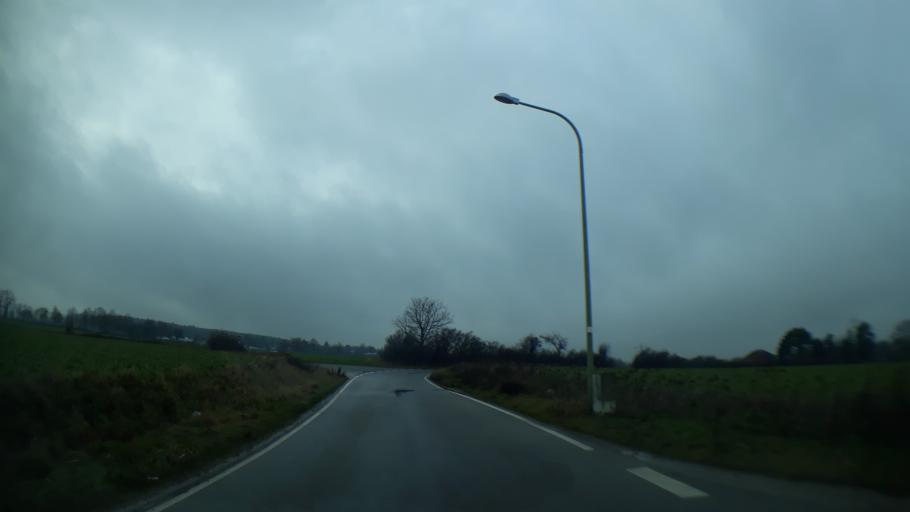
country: DE
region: North Rhine-Westphalia
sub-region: Regierungsbezirk Koln
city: Kreuzau
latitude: 50.7580
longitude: 6.4748
